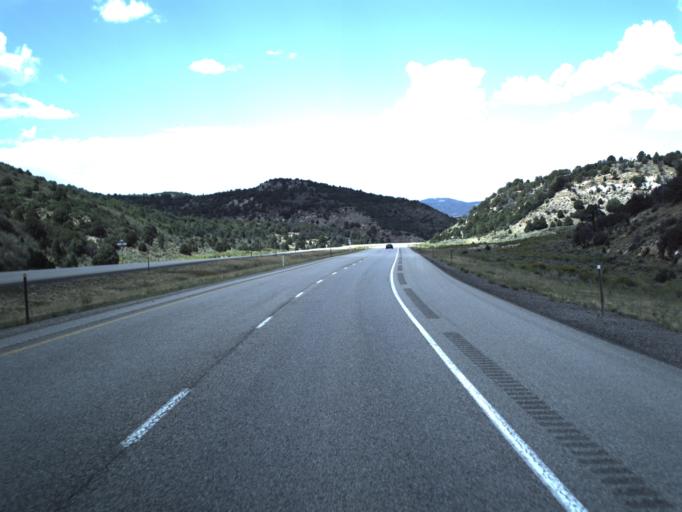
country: US
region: Utah
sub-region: Sevier County
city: Salina
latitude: 38.7847
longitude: -111.4964
